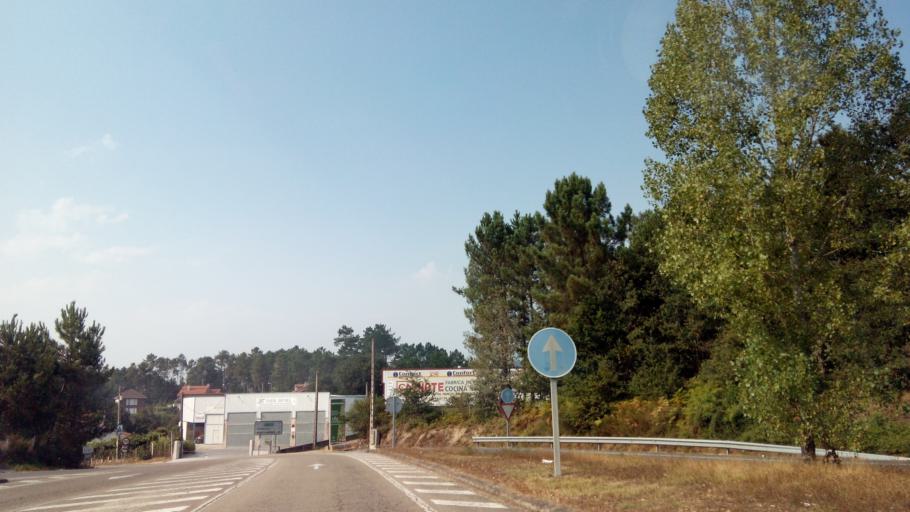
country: ES
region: Galicia
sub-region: Provincia de Pontevedra
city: Ponteareas
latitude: 42.1562
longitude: -8.5012
